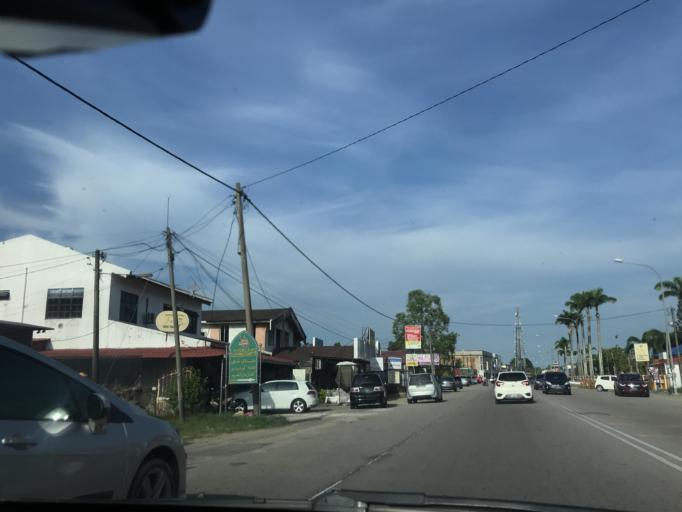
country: MY
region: Kelantan
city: Kota Bharu
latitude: 6.1193
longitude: 102.2896
